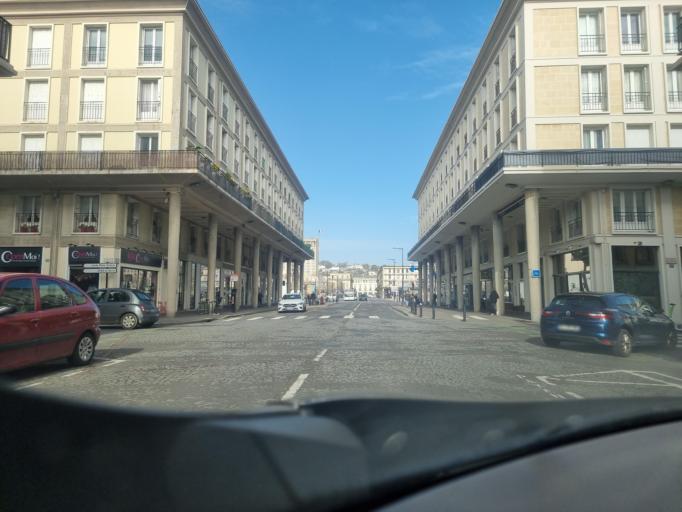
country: FR
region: Haute-Normandie
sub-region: Departement de la Seine-Maritime
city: Le Havre
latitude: 49.4891
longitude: 0.1075
